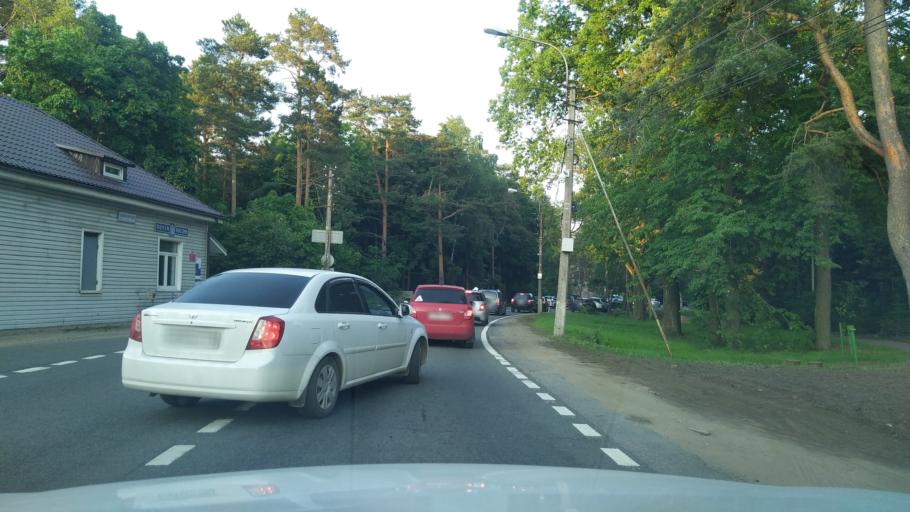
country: RU
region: Leningrad
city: Kurortnyy
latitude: 60.1506
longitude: 29.9239
